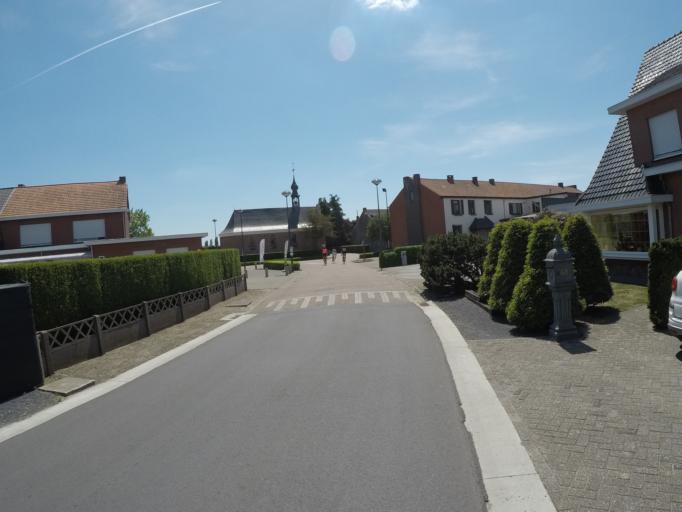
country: BE
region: Flanders
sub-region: Provincie Antwerpen
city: Wuustwezel
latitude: 51.3801
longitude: 4.5606
